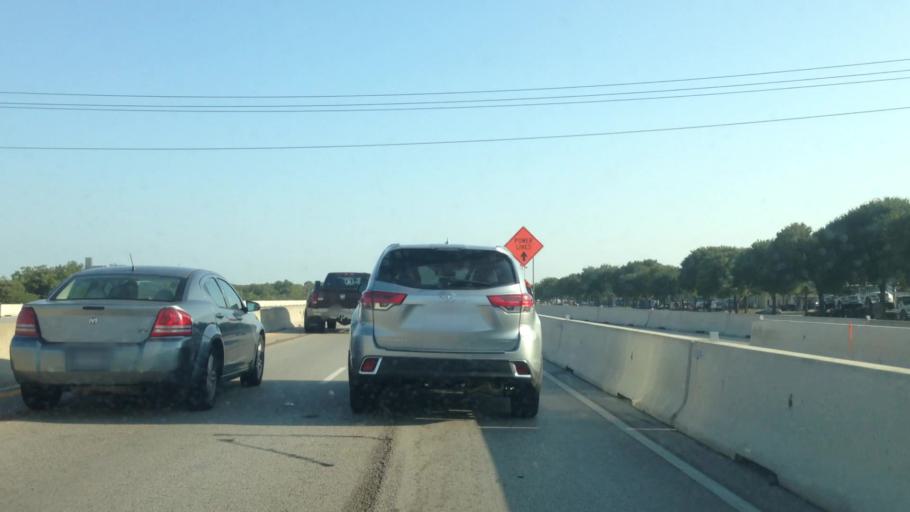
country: US
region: Texas
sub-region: Tarrant County
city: Richland Hills
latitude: 32.7949
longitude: -97.2124
